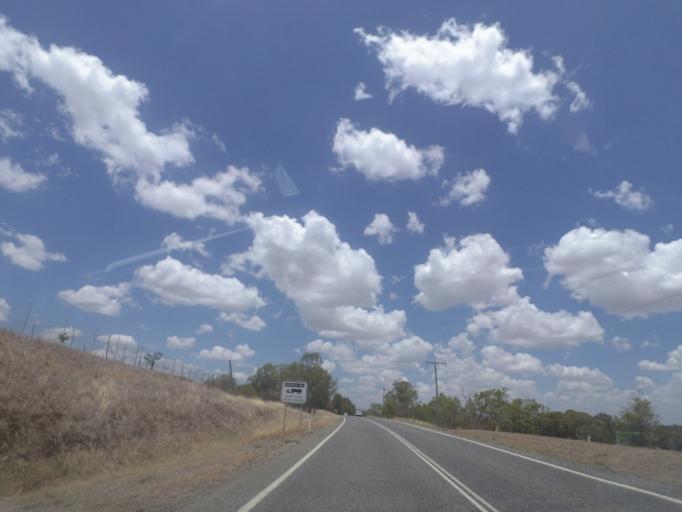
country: AU
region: Queensland
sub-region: Southern Downs
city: Warwick
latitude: -28.0277
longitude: 151.9856
